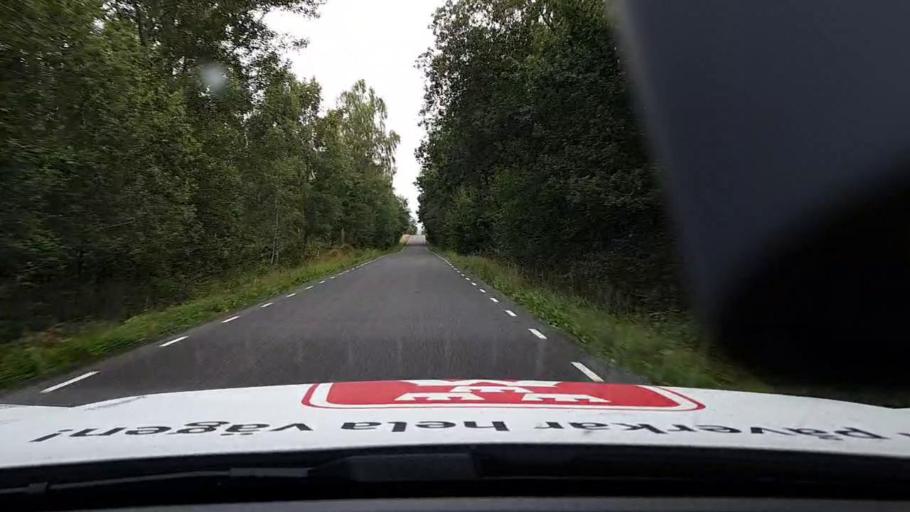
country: SE
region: Skane
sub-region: Hassleholms Kommun
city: Vinslov
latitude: 56.0656
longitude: 13.9009
